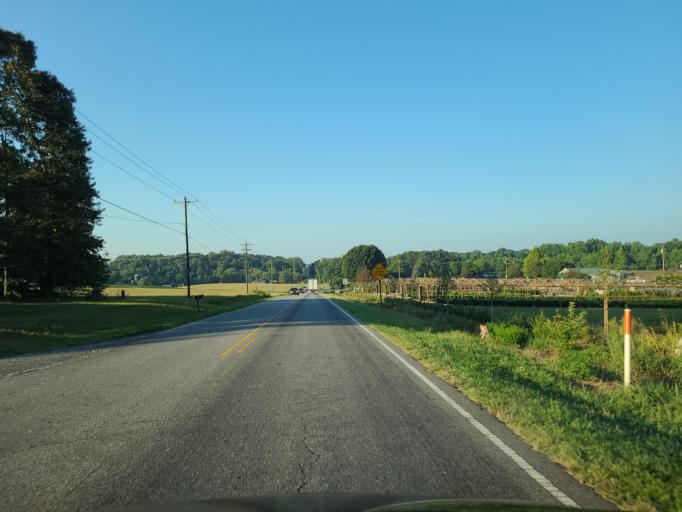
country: US
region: North Carolina
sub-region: Catawba County
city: Mountain View
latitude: 35.6588
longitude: -81.3804
